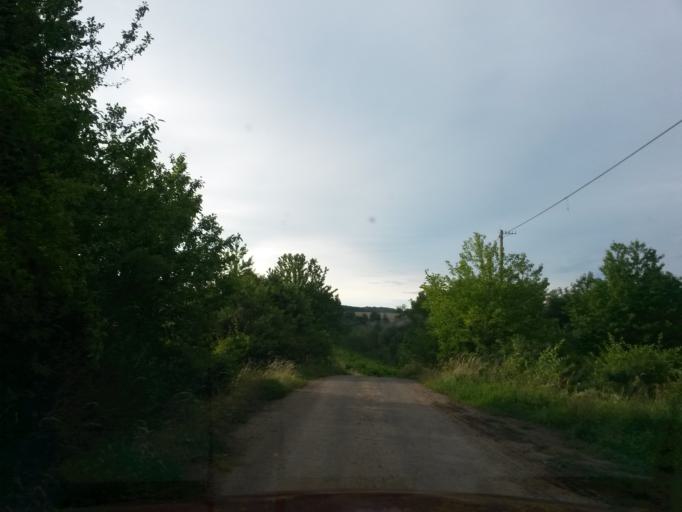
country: SK
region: Banskobystricky
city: Velky Krtis
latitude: 48.3313
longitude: 19.4358
